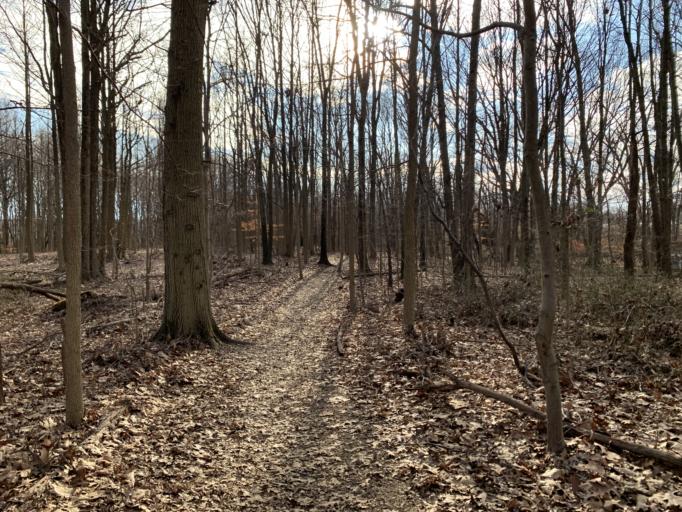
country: US
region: New York
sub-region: Richmond County
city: Staten Island
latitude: 40.5767
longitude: -74.1444
